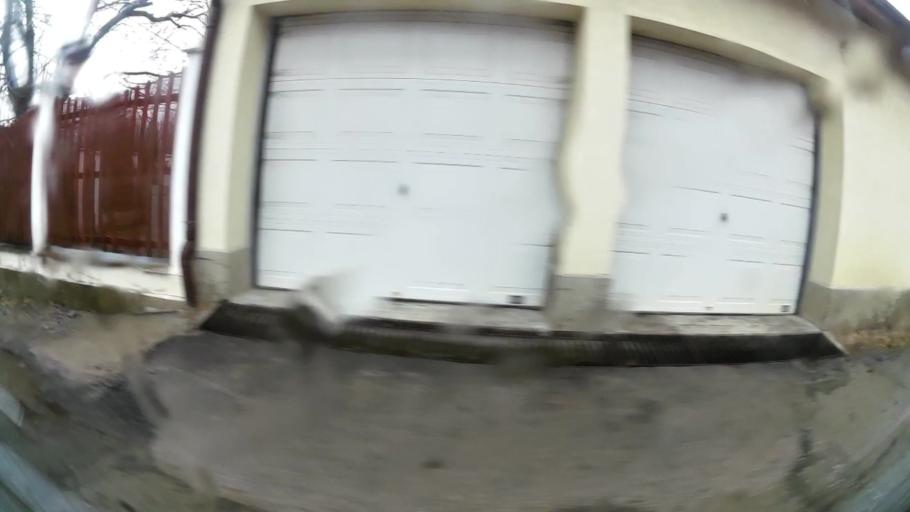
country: BG
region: Sofia-Capital
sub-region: Stolichna Obshtina
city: Sofia
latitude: 42.6287
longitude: 23.3664
